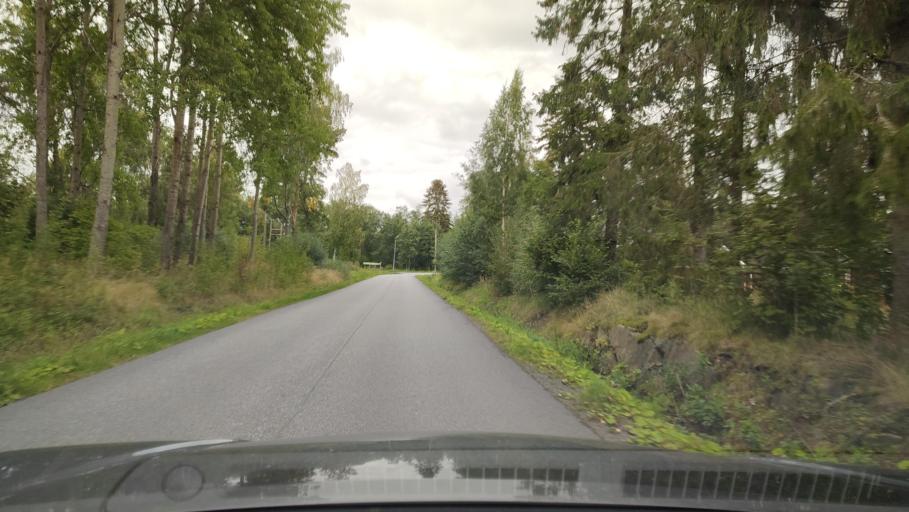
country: FI
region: Ostrobothnia
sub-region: Sydosterbotten
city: Kristinestad
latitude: 62.2628
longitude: 21.3607
